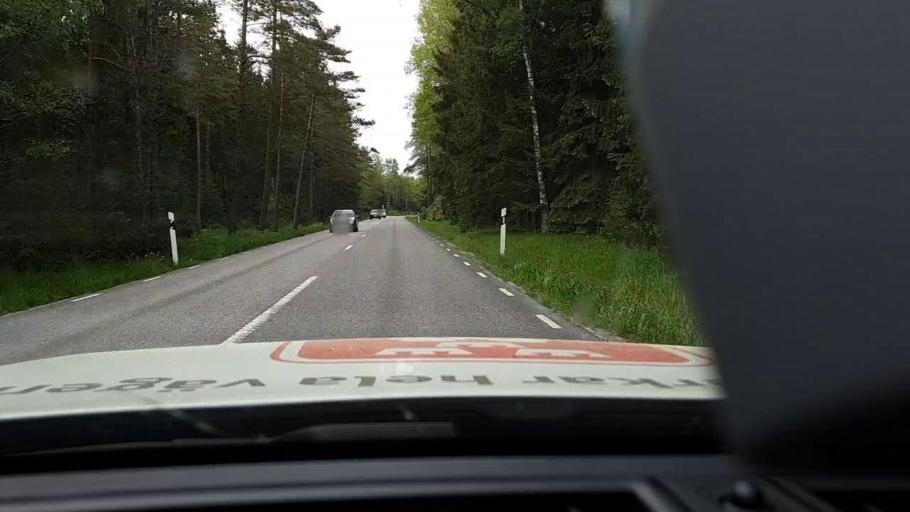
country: SE
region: Stockholm
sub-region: Haninge Kommun
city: Haninge
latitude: 59.1480
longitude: 18.1804
